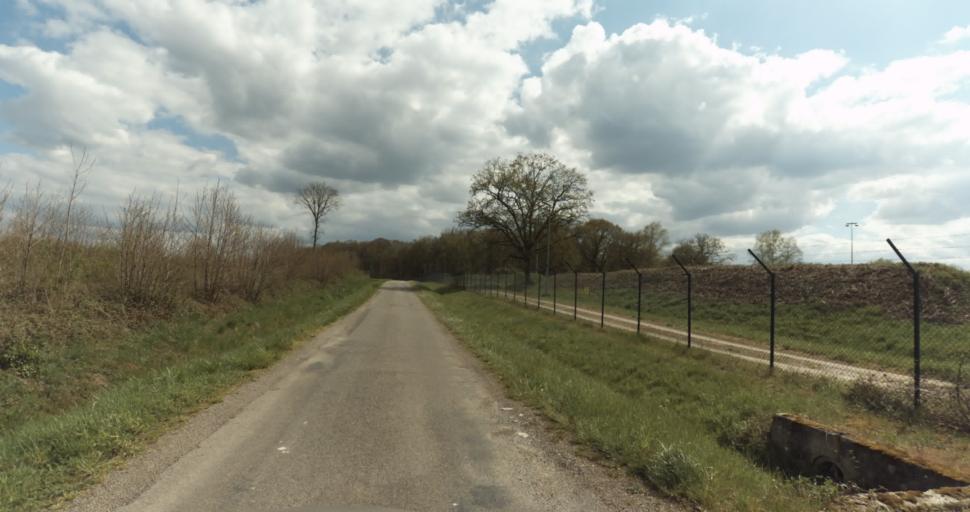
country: FR
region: Bourgogne
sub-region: Departement de la Cote-d'Or
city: Auxonne
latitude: 47.1771
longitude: 5.4096
